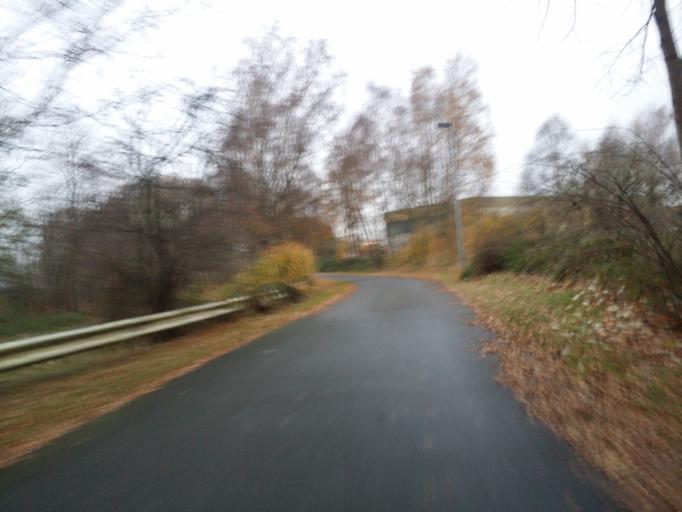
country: DE
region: Bremen
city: Bremen
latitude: 53.0249
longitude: 8.8021
